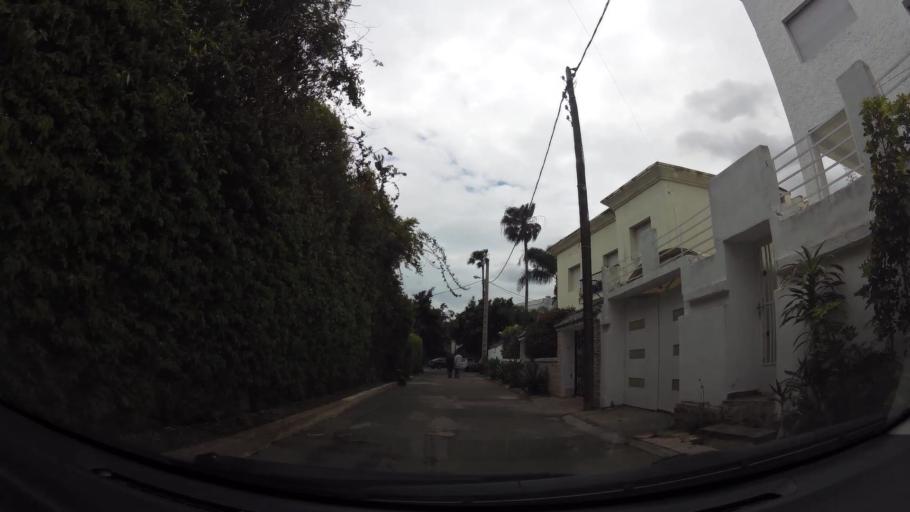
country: MA
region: Grand Casablanca
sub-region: Casablanca
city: Casablanca
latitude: 33.5768
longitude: -7.6570
